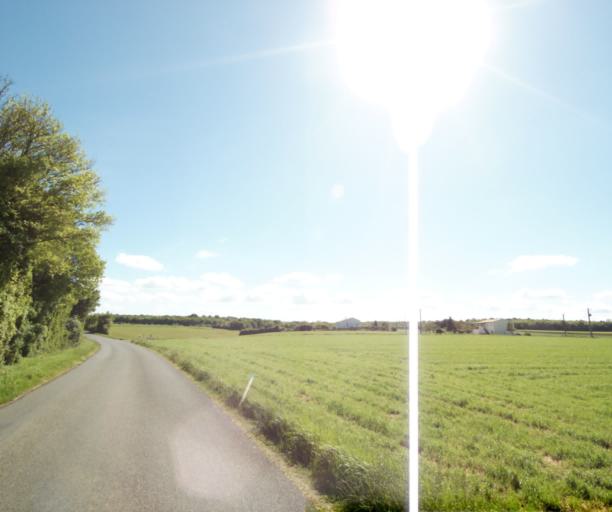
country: FR
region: Poitou-Charentes
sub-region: Departement de la Charente-Maritime
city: Bussac-sur-Charente
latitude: 45.8152
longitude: -0.6621
